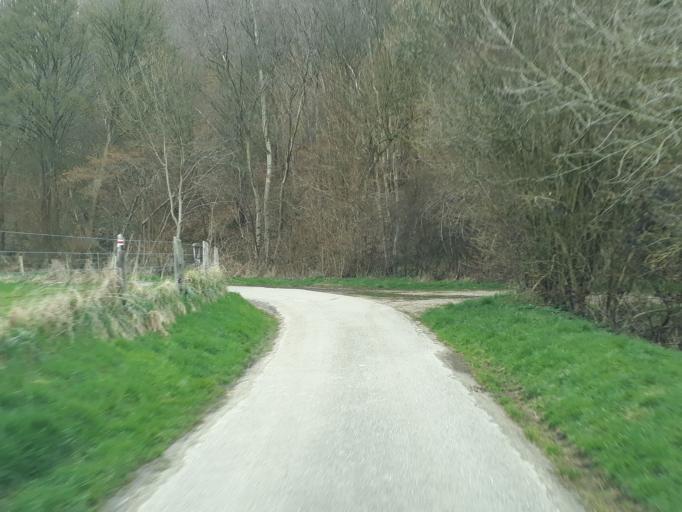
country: FR
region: Haute-Normandie
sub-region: Departement de la Seine-Maritime
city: Les Loges
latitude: 49.6761
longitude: 0.2643
